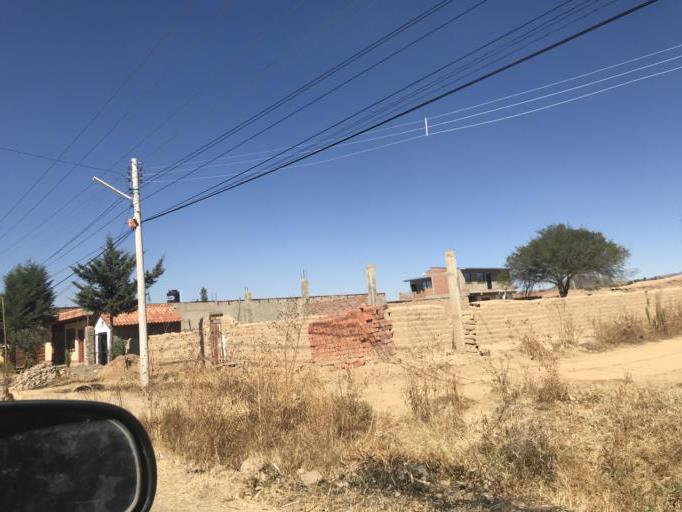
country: BO
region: Cochabamba
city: Tarata
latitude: -17.6024
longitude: -65.9800
